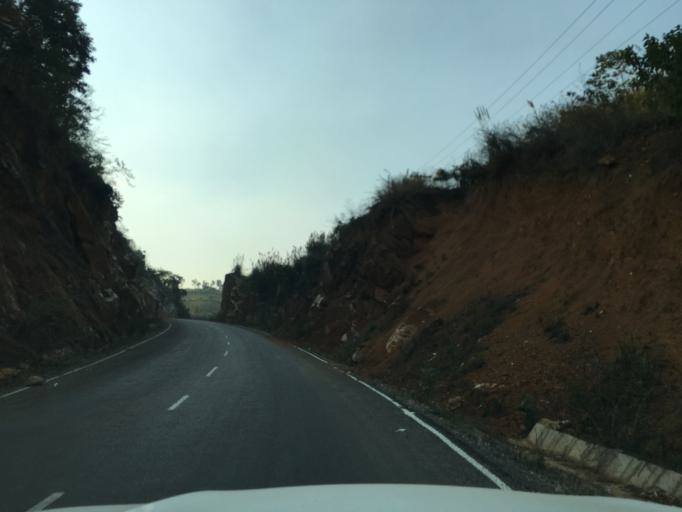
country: LA
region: Houaphan
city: Xam Nua
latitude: 20.5694
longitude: 104.0605
